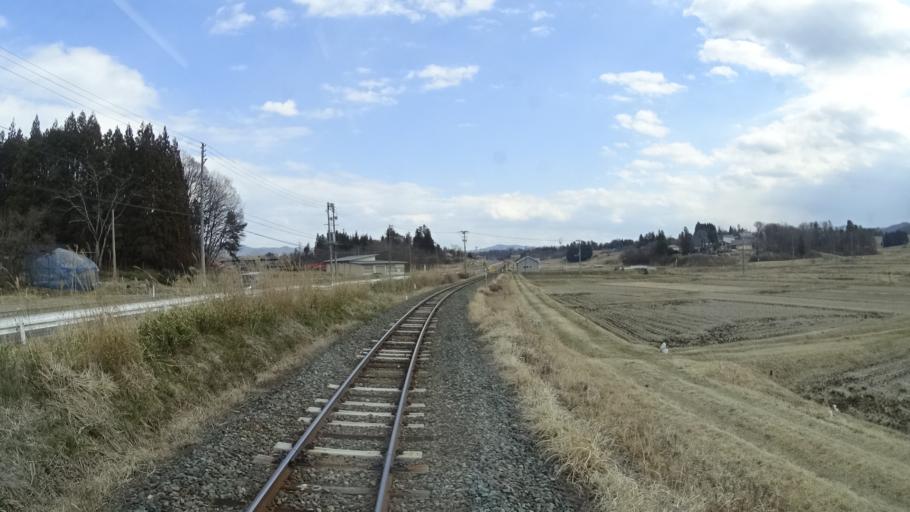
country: JP
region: Iwate
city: Hanamaki
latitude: 39.4057
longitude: 141.2011
